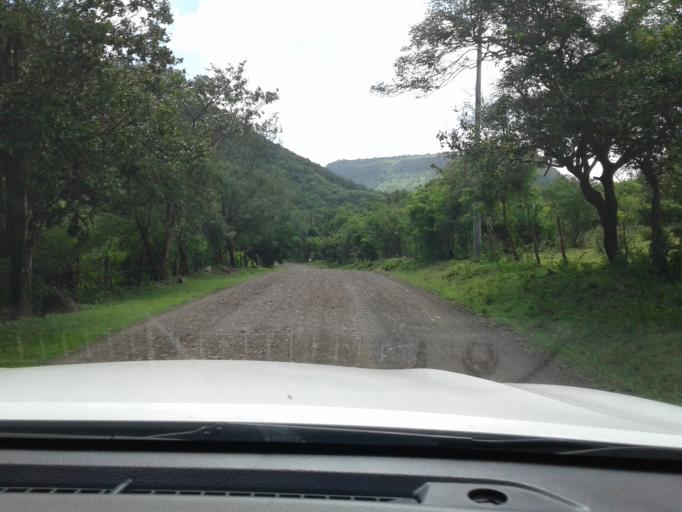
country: NI
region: Matagalpa
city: Terrabona
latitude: 12.8479
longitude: -86.0434
